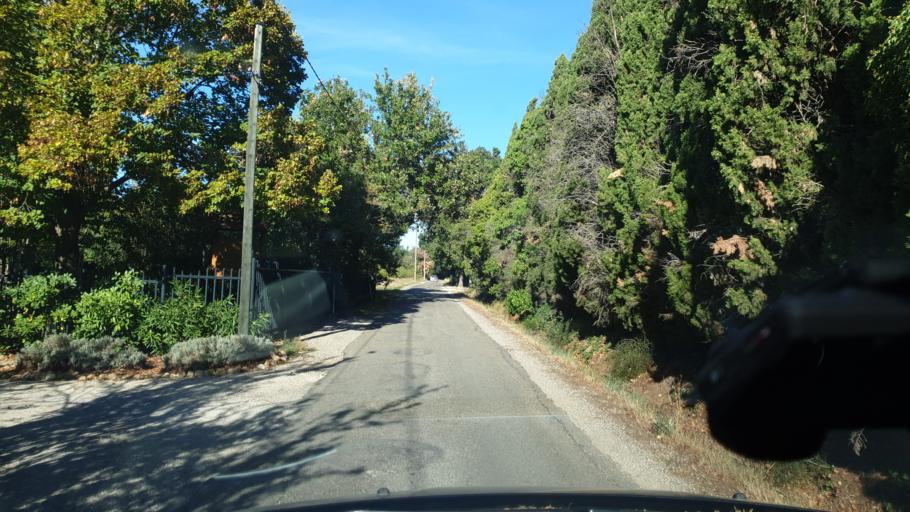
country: FR
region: Provence-Alpes-Cote d'Azur
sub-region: Departement du Vaucluse
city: Monteux
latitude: 44.0476
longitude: 5.0147
